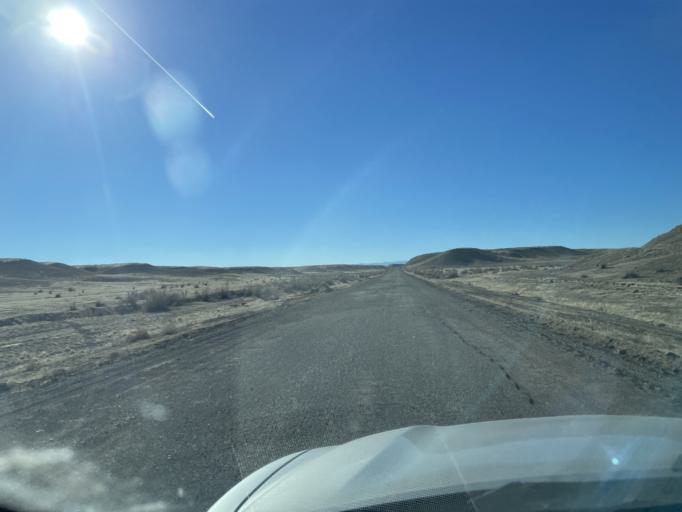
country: US
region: Colorado
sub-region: Mesa County
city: Loma
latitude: 39.2059
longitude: -109.0849
